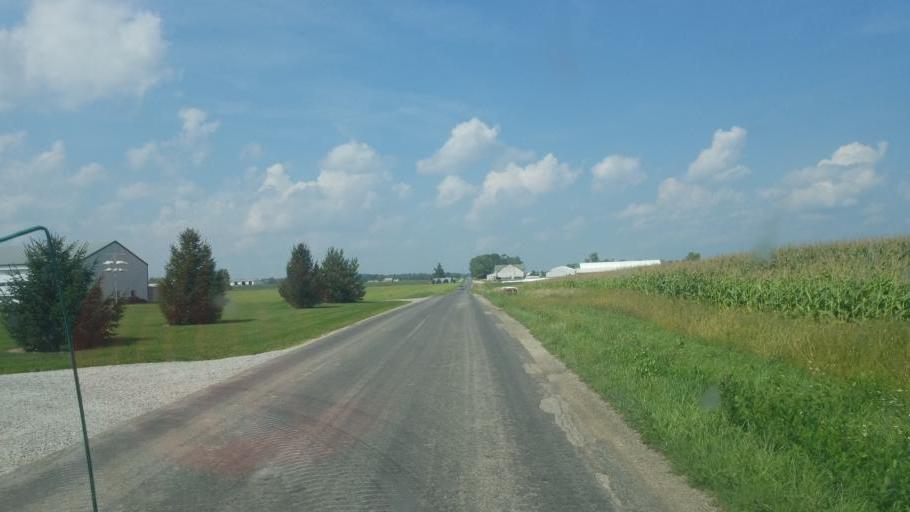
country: US
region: Ohio
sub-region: Huron County
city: Greenwich
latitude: 40.9434
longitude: -82.4540
